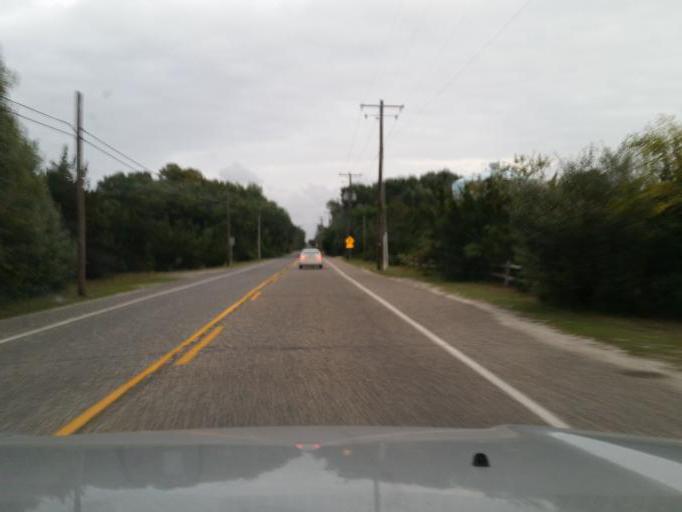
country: US
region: New Jersey
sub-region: Cape May County
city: West Cape May
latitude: 38.9434
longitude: -74.9654
